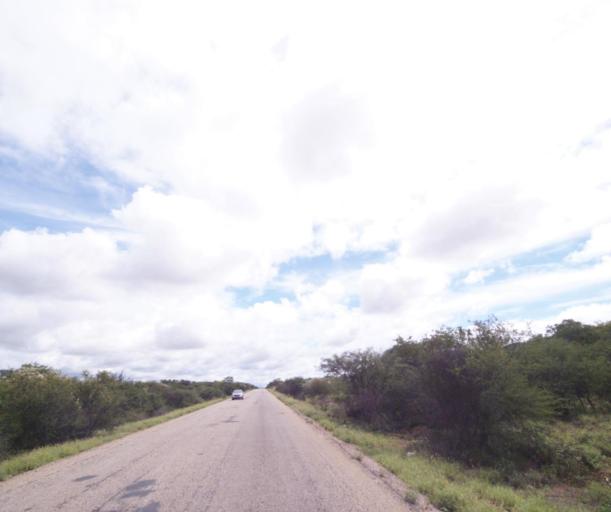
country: BR
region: Bahia
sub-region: Brumado
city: Brumado
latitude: -14.1896
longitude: -41.5767
